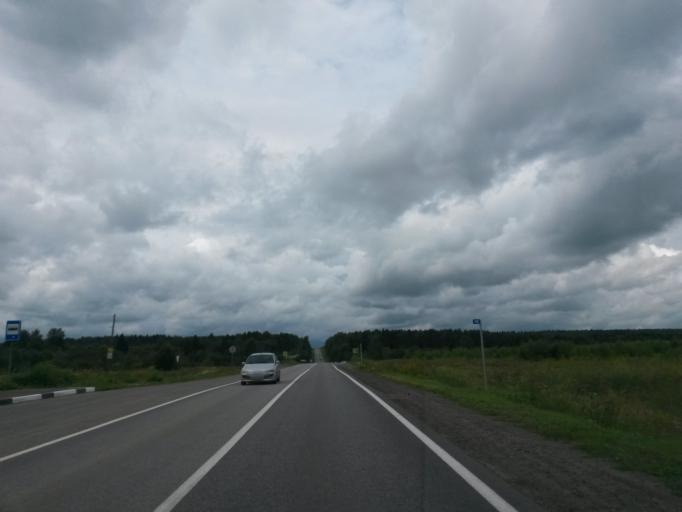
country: RU
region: Jaroslavl
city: Konstantinovskiy
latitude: 57.8127
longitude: 39.7256
